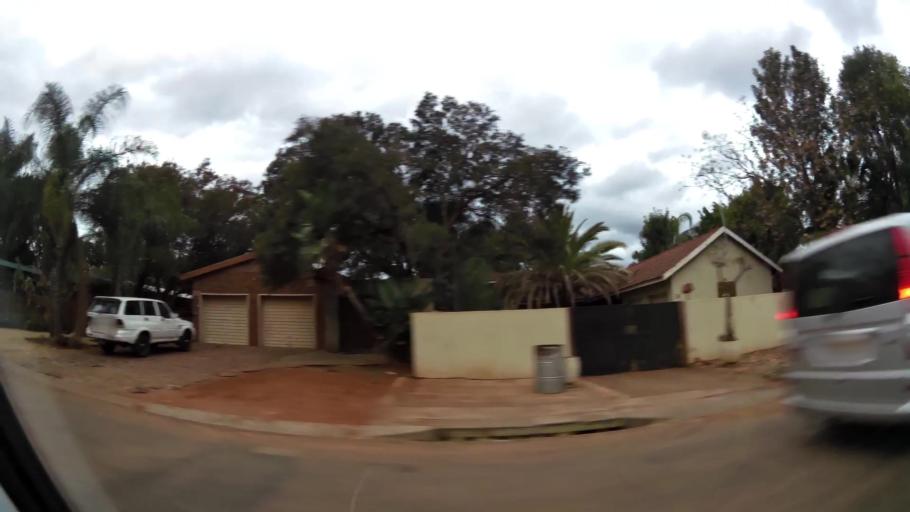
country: ZA
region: Limpopo
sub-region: Waterberg District Municipality
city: Mokopane
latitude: -24.1855
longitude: 28.9914
